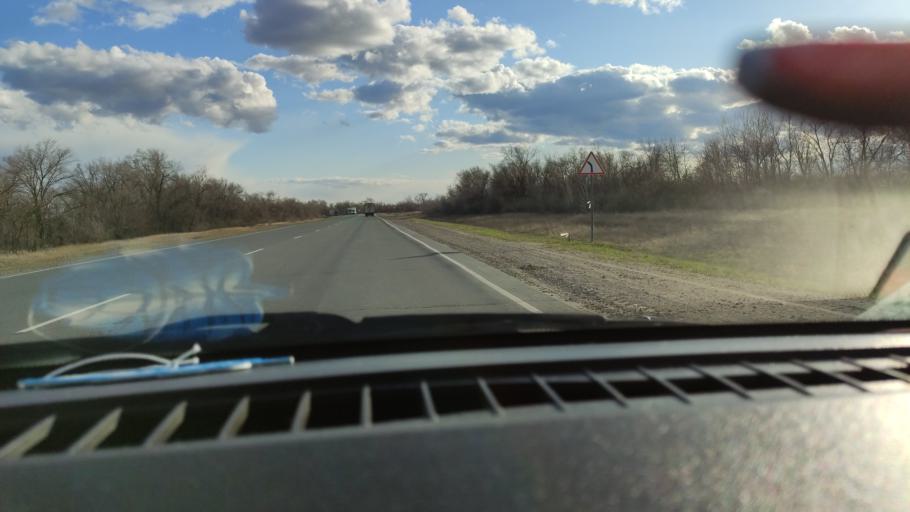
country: RU
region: Saratov
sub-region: Saratovskiy Rayon
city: Saratov
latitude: 51.7072
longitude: 46.0148
